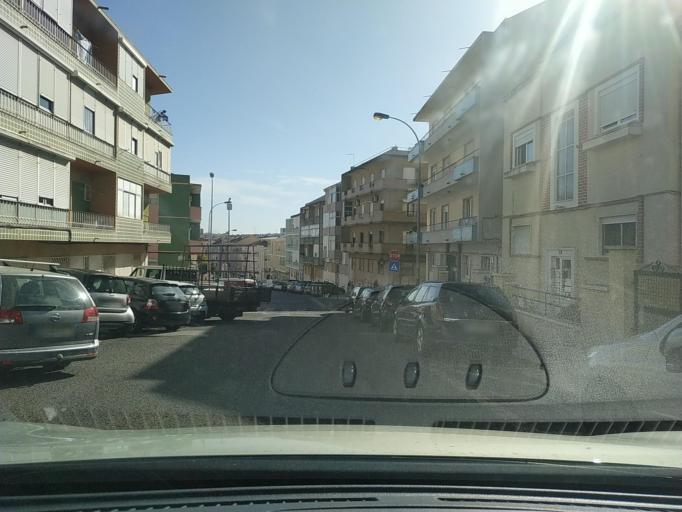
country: PT
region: Lisbon
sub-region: Amadora
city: Amadora
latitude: 38.7636
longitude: -9.2372
